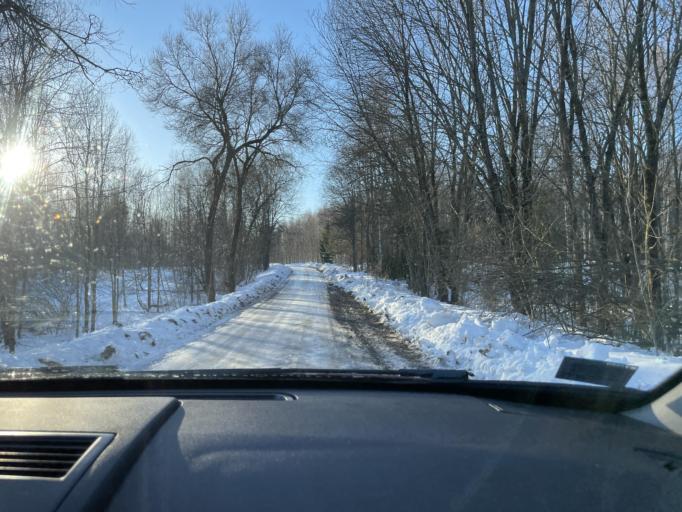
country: LV
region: Ludzas Rajons
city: Ludza
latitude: 56.4526
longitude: 27.6357
